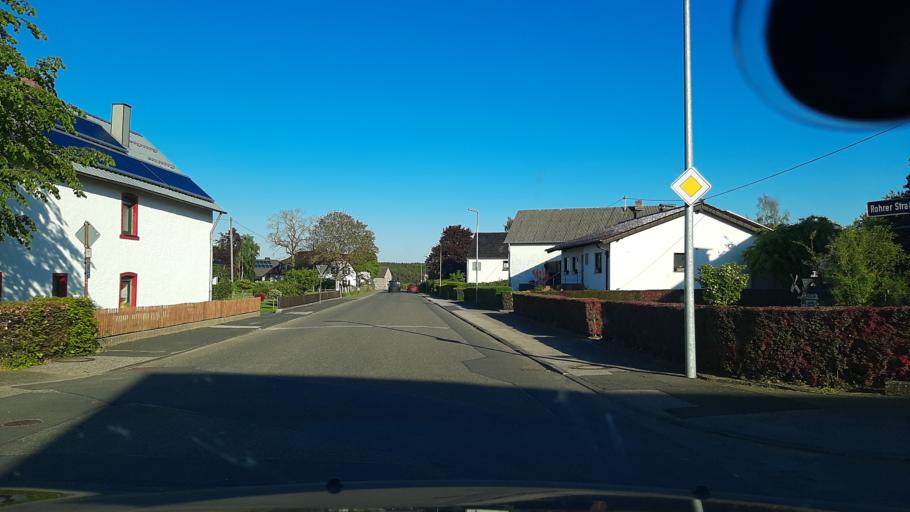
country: DE
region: Rheinland-Pfalz
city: Ohlenhard
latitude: 50.4738
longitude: 6.7155
